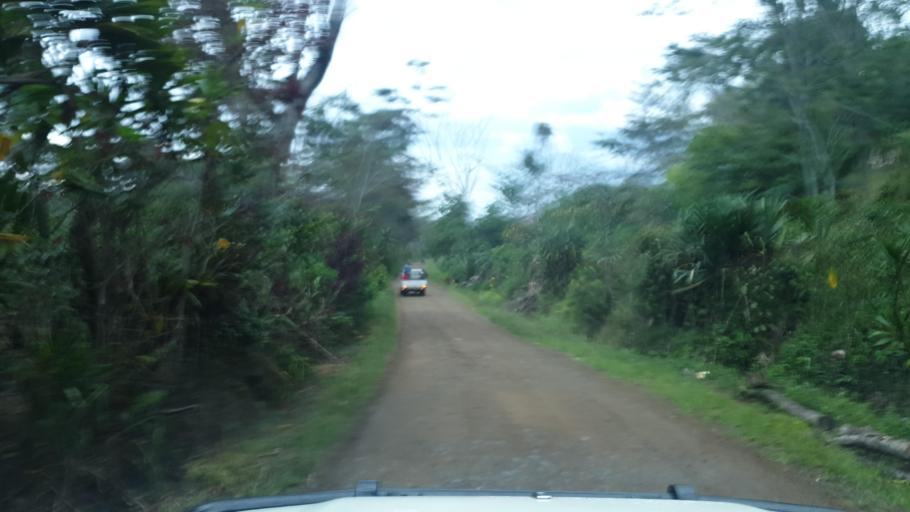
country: PG
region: Eastern Highlands
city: Goroka
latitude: -5.9720
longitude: 145.2762
